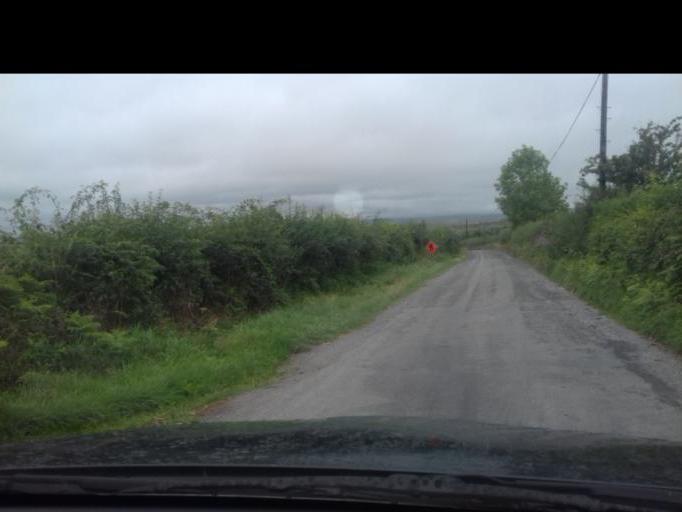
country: IE
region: Leinster
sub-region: Kilkenny
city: Graiguenamanagh
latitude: 52.5983
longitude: -7.0123
